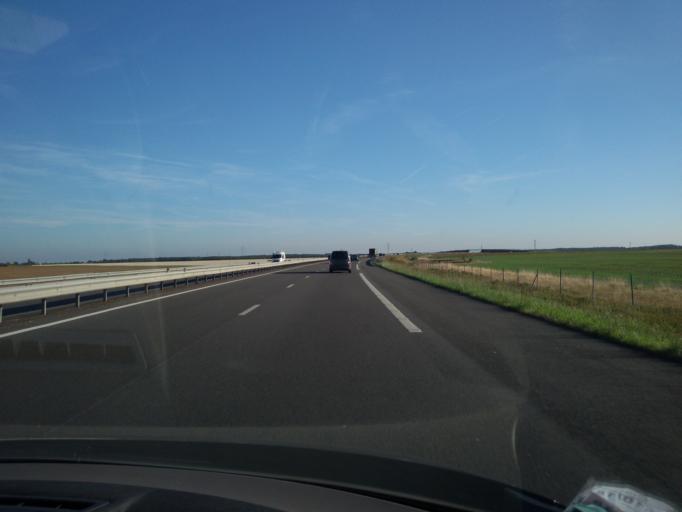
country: FR
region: Centre
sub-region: Departement du Cher
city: Levet
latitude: 46.9516
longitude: 2.4168
